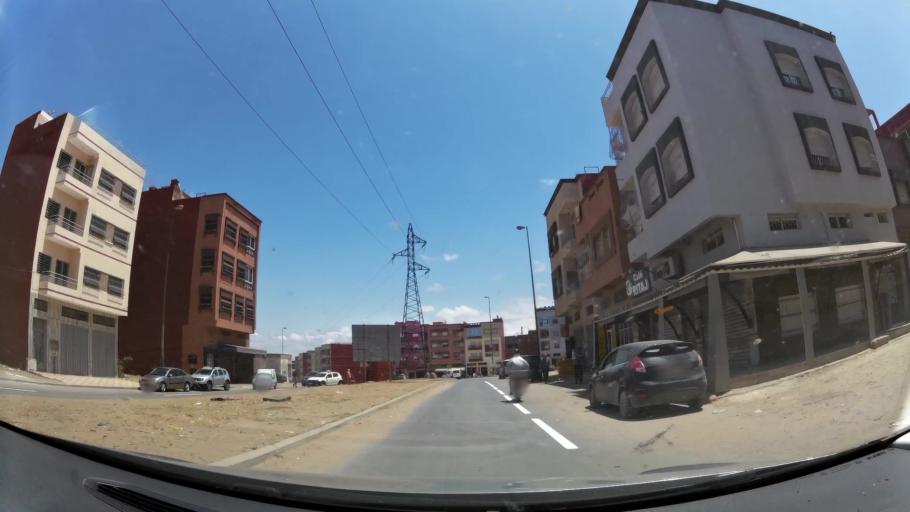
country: MA
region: Gharb-Chrarda-Beni Hssen
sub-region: Kenitra Province
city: Kenitra
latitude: 34.2343
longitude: -6.6174
